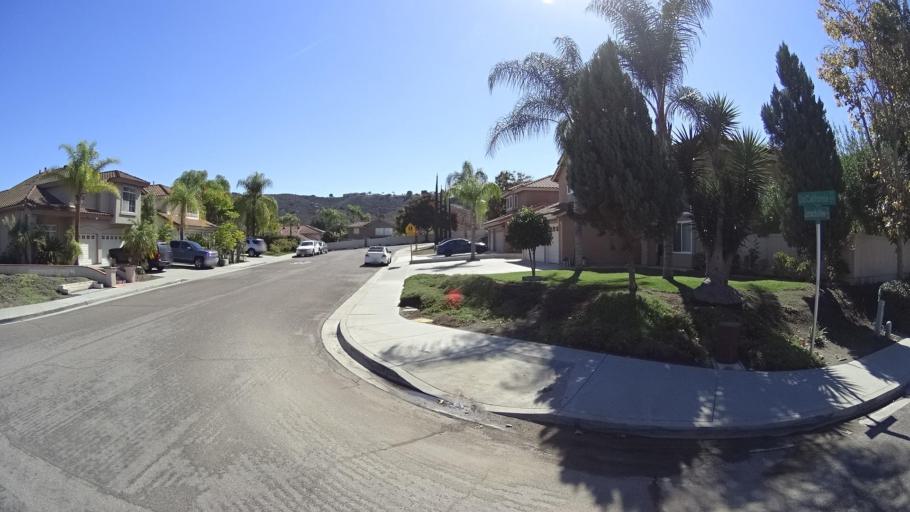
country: US
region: California
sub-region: San Diego County
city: Rancho San Diego
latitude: 32.7368
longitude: -116.9149
